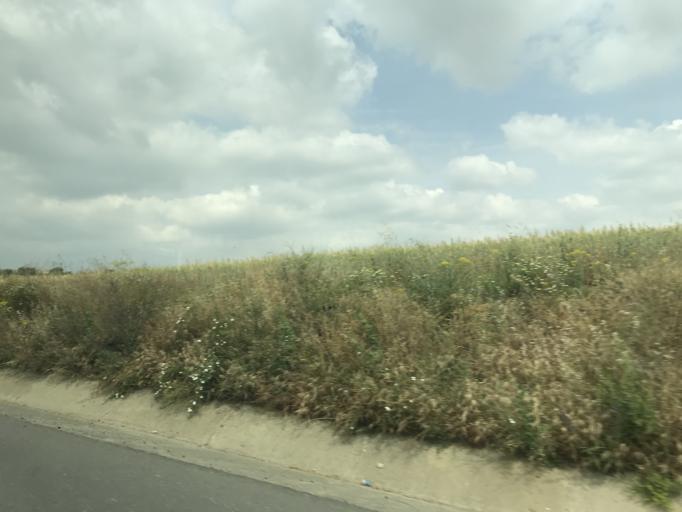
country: TR
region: Tekirdag
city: Tekirdag
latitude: 40.9918
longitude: 27.5651
